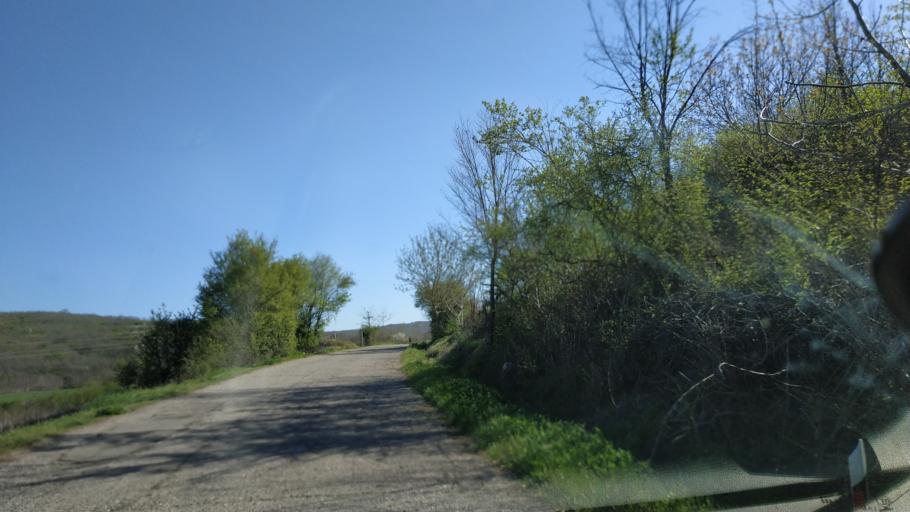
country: RS
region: Central Serbia
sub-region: Nisavski Okrug
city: Aleksinac
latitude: 43.4977
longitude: 21.6749
